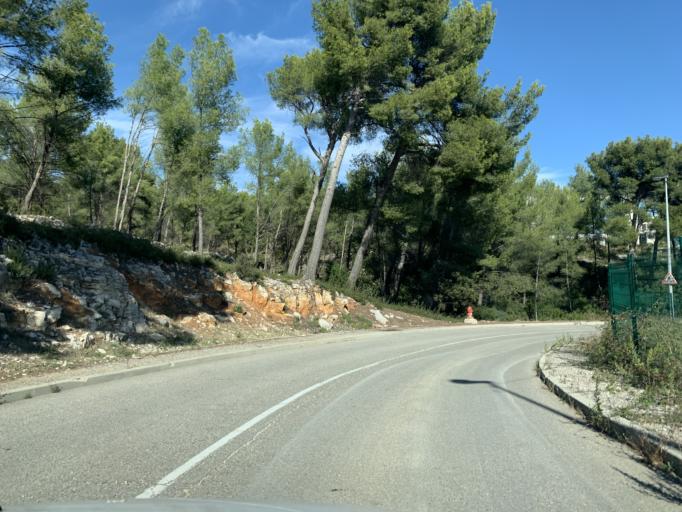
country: FR
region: Provence-Alpes-Cote d'Azur
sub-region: Departement des Bouches-du-Rhone
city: La Ciotat
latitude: 43.2082
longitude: 5.5963
